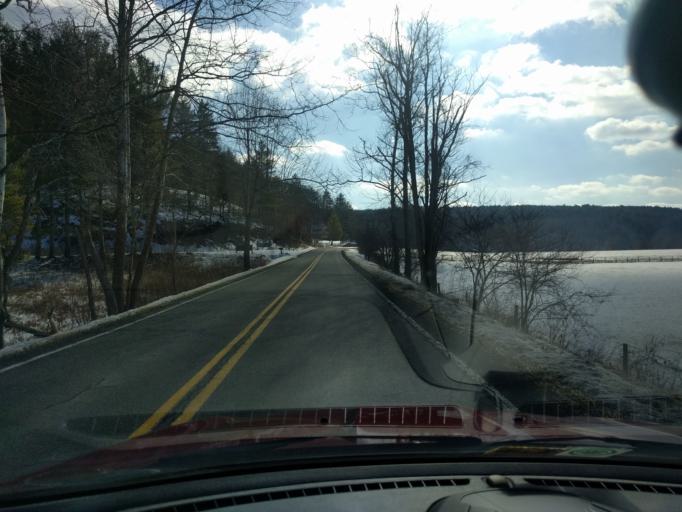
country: US
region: Virginia
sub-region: Bath County
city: Warm Springs
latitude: 38.0765
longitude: -79.8440
